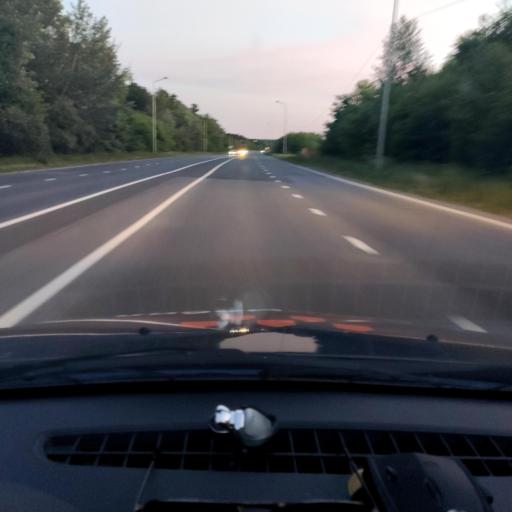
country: RU
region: Belgorod
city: Staryy Oskol
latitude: 51.3514
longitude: 37.8285
